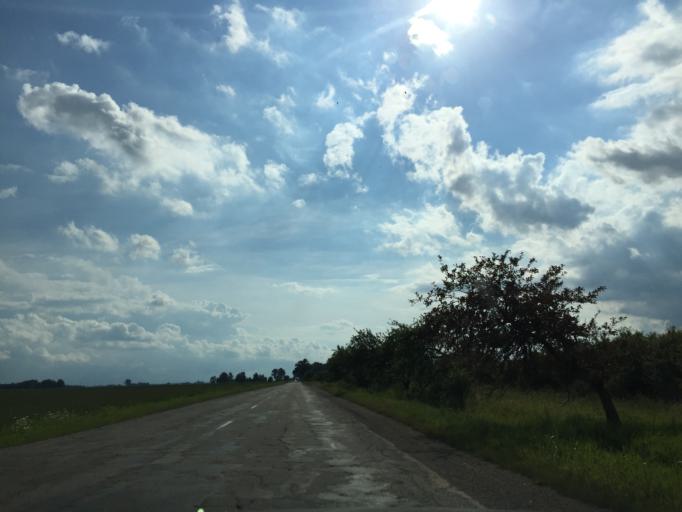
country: LV
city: Tervete
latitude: 56.5863
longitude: 23.4591
